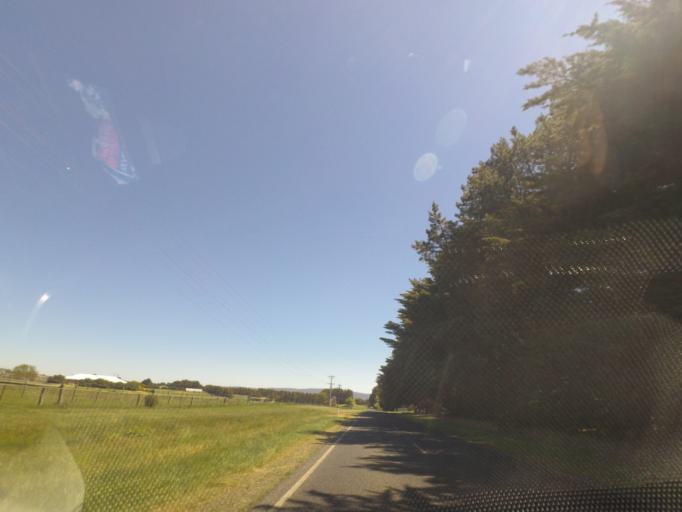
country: AU
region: Victoria
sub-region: Hume
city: Sunbury
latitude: -37.2812
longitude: 144.7507
